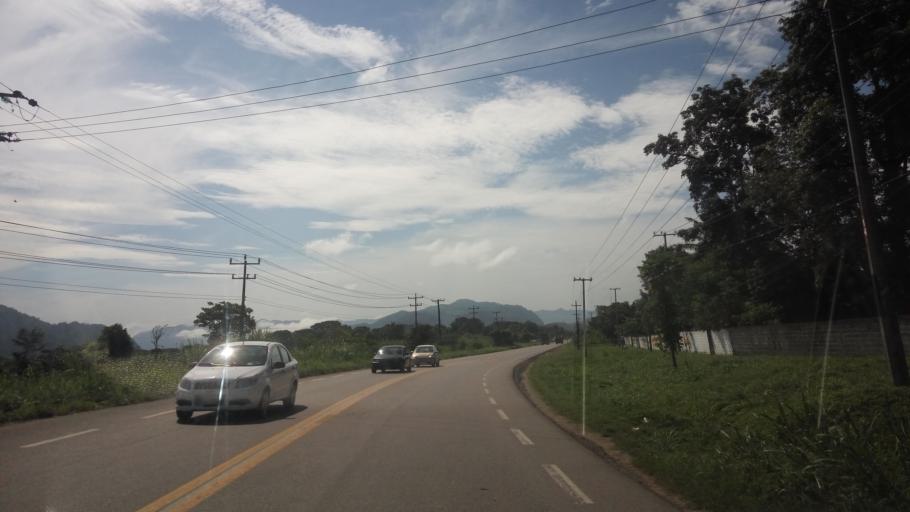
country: MX
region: Tabasco
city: Teapa
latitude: 17.5777
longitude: -92.9602
